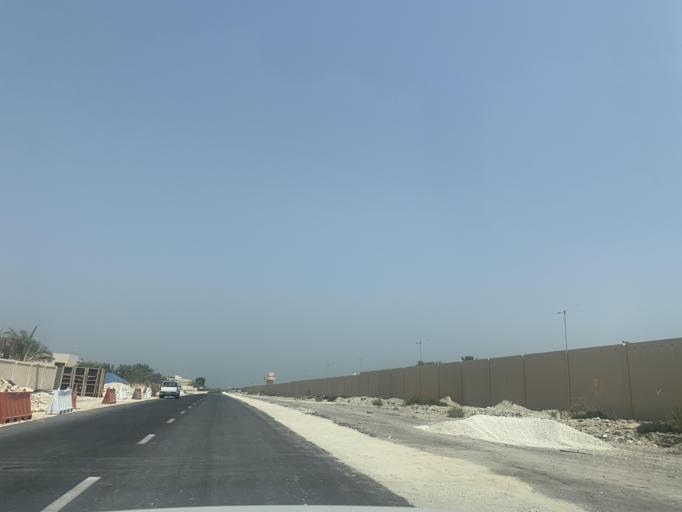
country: BH
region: Central Governorate
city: Madinat Hamad
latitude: 26.1486
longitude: 50.4773
